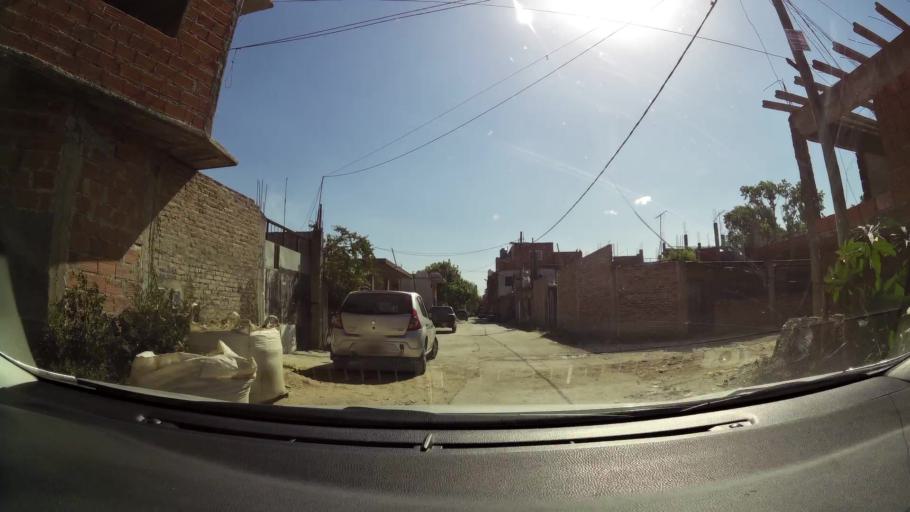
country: AR
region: Buenos Aires F.D.
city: Villa Lugano
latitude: -34.7101
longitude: -58.4786
